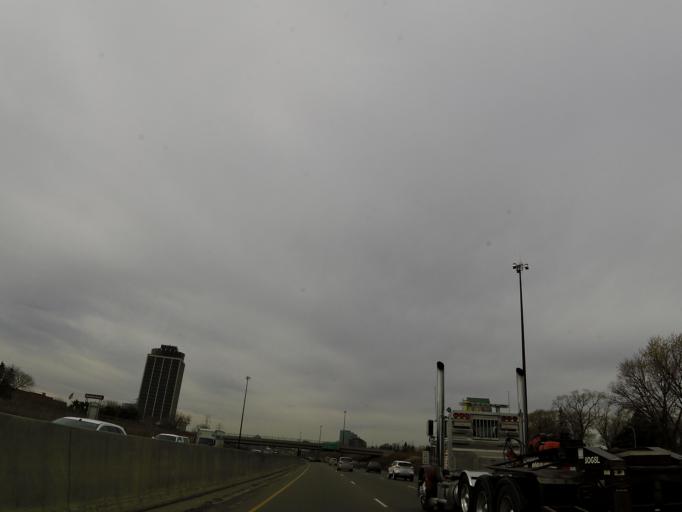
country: US
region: Minnesota
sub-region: Hennepin County
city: Bloomington
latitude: 44.8618
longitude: -93.3156
